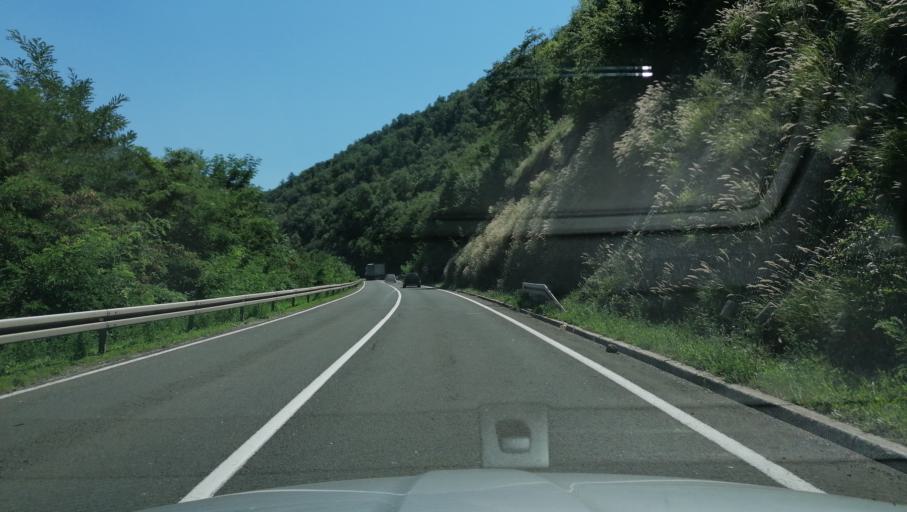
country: RS
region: Central Serbia
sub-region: Raski Okrug
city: Kraljevo
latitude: 43.5904
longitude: 20.5723
